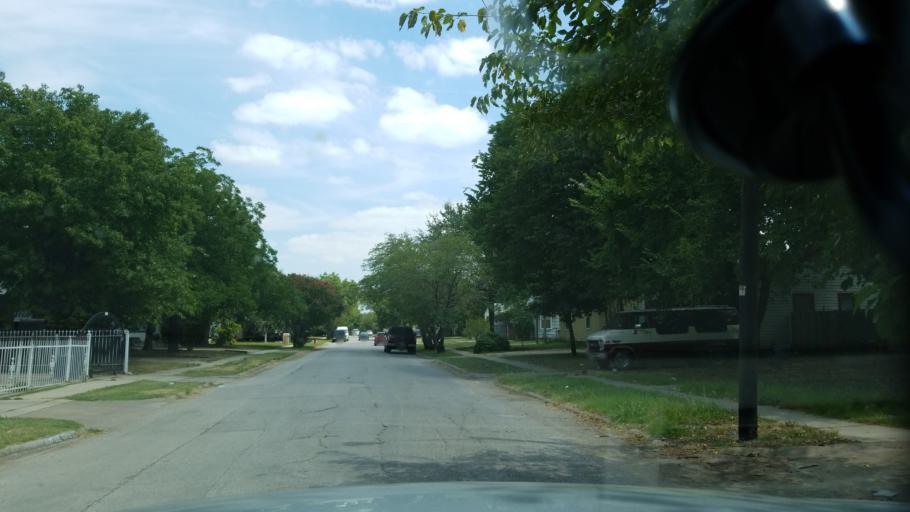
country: US
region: Texas
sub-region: Dallas County
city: Grand Prairie
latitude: 32.7537
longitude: -96.9809
